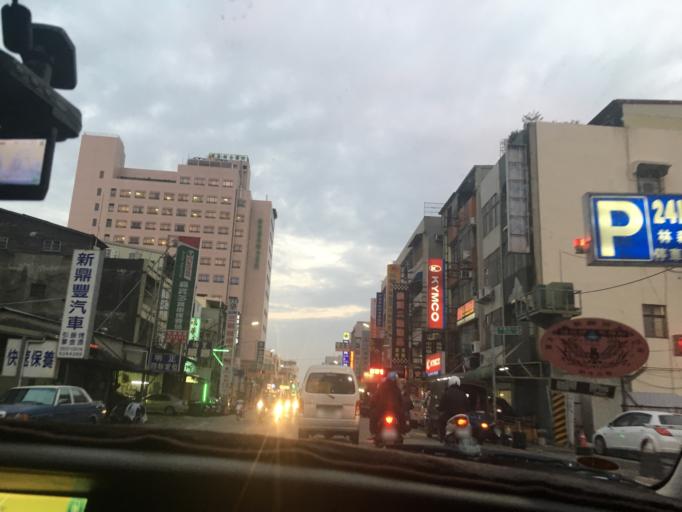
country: TW
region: Taiwan
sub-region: Hsinchu
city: Hsinchu
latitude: 24.7973
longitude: 120.9640
